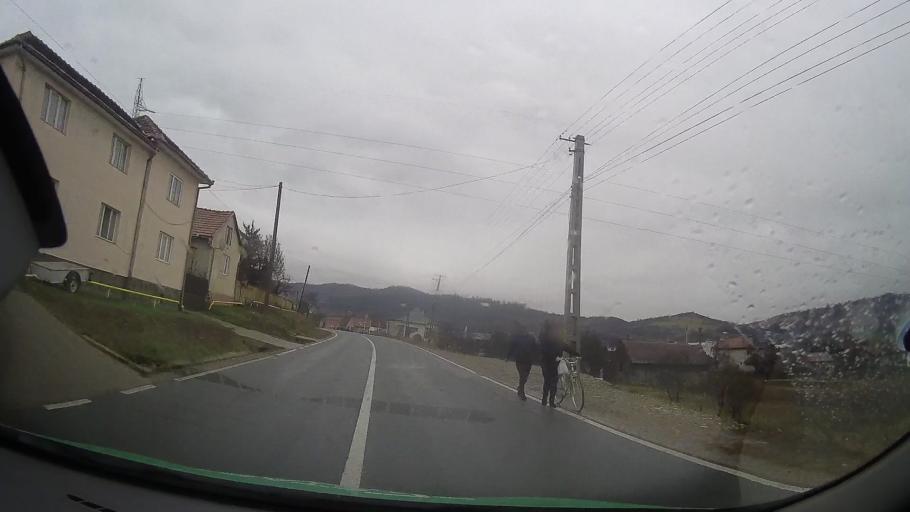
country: RO
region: Bistrita-Nasaud
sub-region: Comuna Teaca
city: Teaca
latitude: 46.9140
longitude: 24.4979
